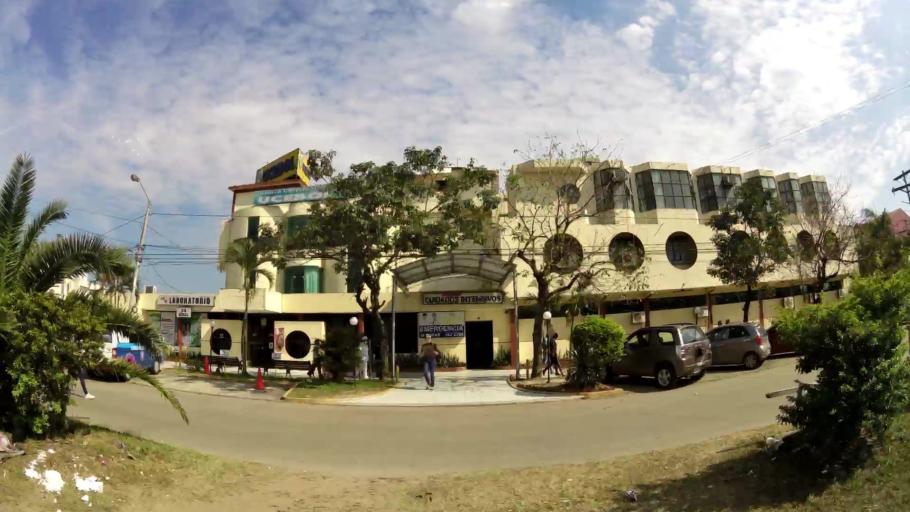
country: BO
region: Santa Cruz
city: Santa Cruz de la Sierra
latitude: -17.7313
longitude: -63.1694
